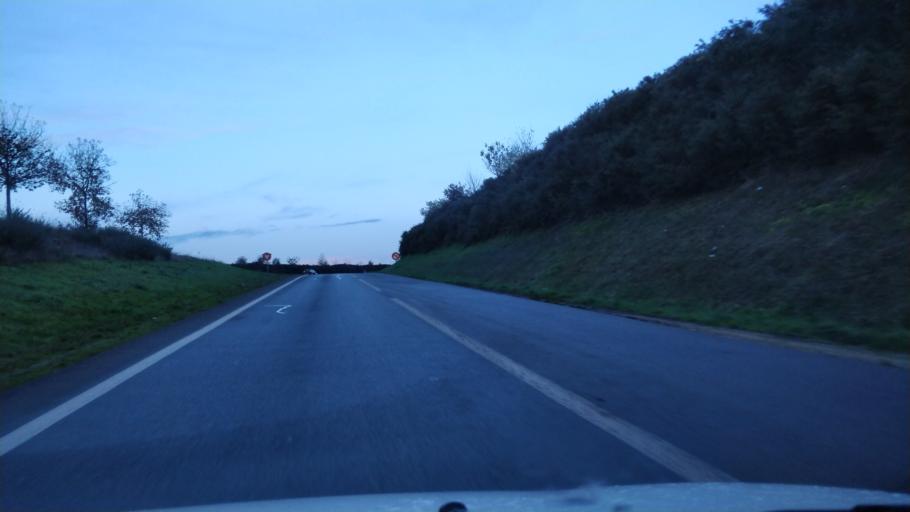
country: FR
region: Brittany
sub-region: Departement du Morbihan
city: Pontivy
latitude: 48.0807
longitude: -2.9395
